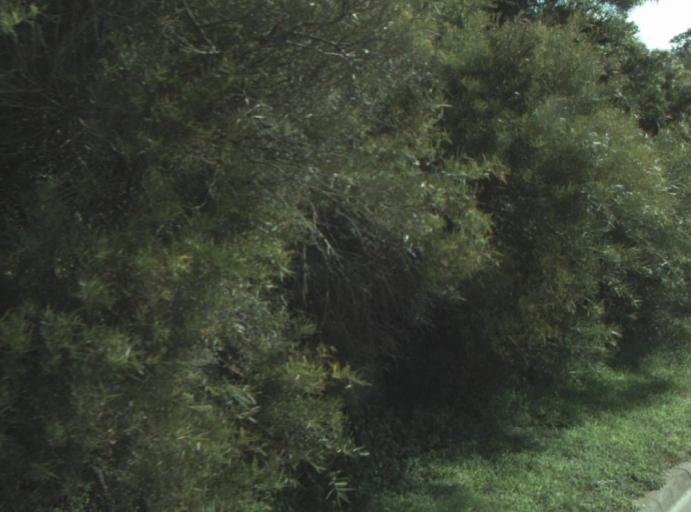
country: AU
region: Victoria
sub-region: Greater Geelong
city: Lara
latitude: -38.0202
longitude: 144.4013
